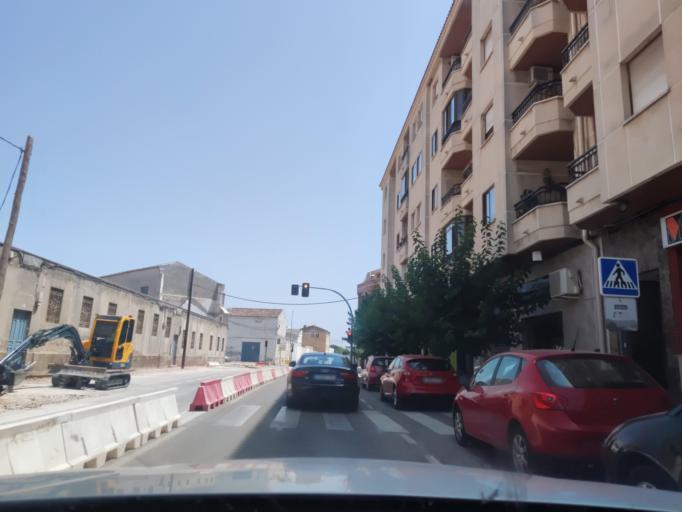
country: ES
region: Castille-La Mancha
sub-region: Provincia de Albacete
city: Hellin
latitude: 38.5092
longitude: -1.6914
